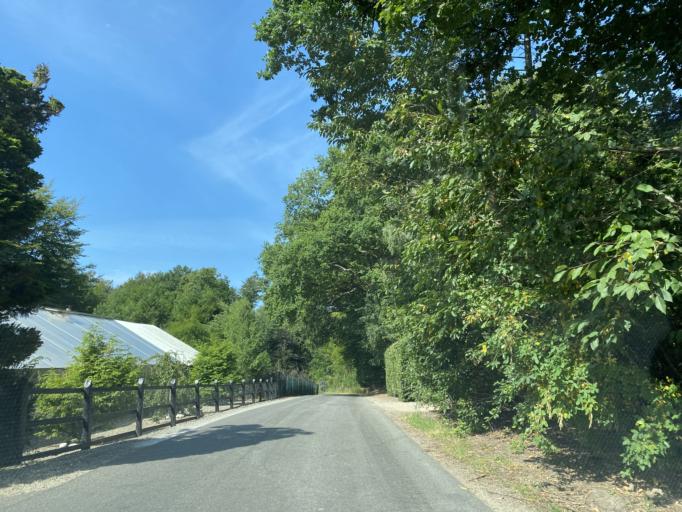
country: DK
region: Central Jutland
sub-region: Favrskov Kommune
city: Hammel
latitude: 56.2537
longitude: 9.8241
